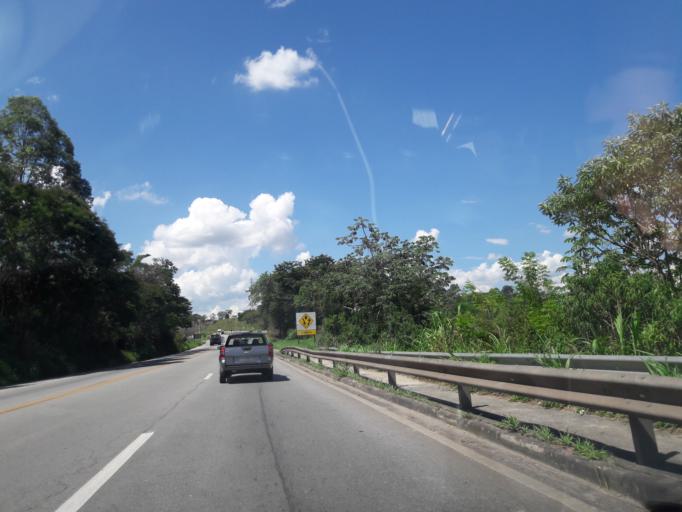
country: BR
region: Sao Paulo
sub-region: Cajamar
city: Cajamar
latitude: -23.3419
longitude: -46.8300
